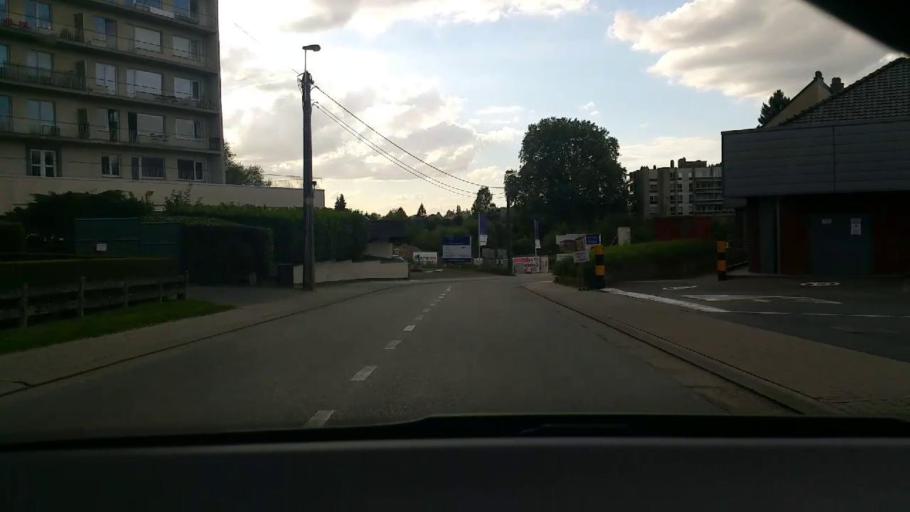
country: BE
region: Wallonia
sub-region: Province du Brabant Wallon
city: Nivelles
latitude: 50.5953
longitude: 4.3372
